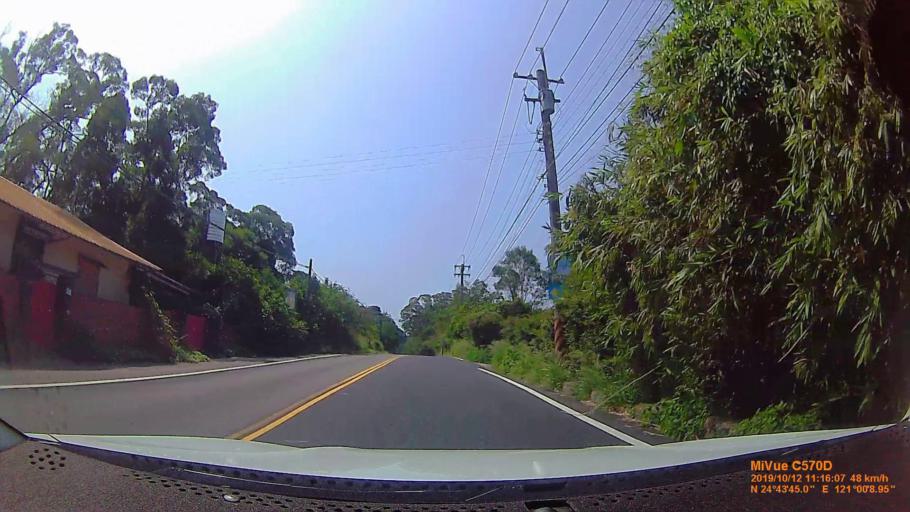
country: TW
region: Taiwan
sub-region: Hsinchu
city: Hsinchu
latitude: 24.7291
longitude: 121.0024
